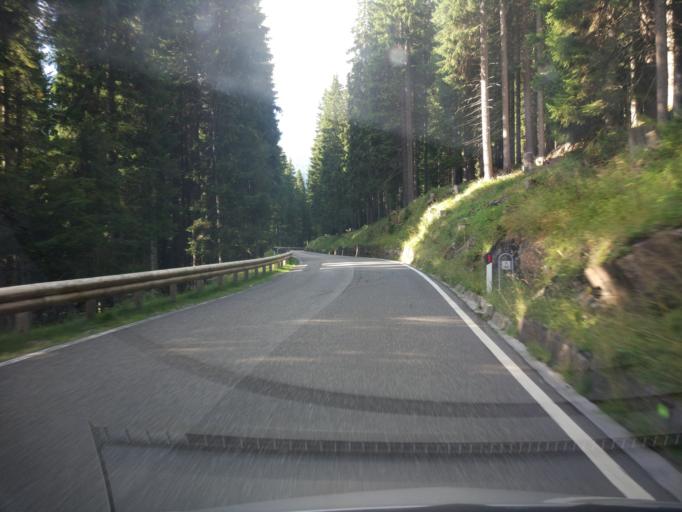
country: IT
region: Veneto
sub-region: Provincia di Belluno
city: Falcade Alto
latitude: 46.2976
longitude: 11.7624
